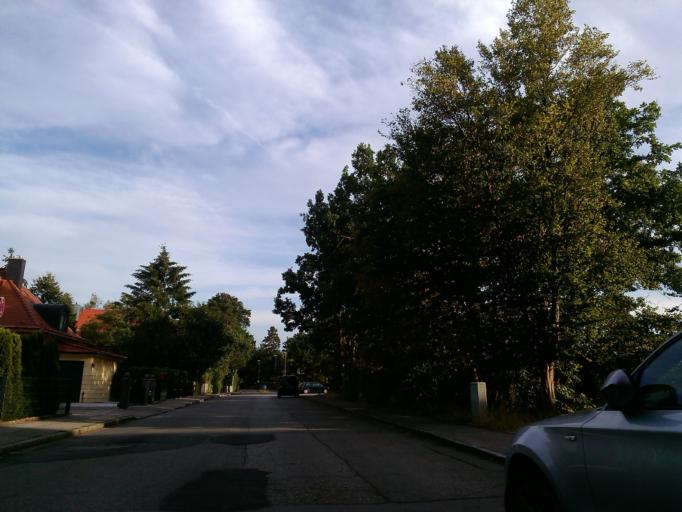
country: DE
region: Bavaria
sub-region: Upper Bavaria
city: Gauting
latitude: 48.0788
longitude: 11.3773
